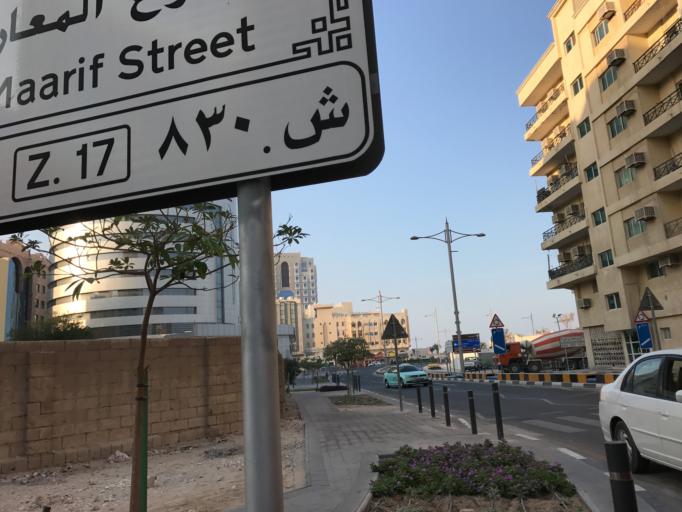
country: QA
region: Baladiyat ad Dawhah
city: Doha
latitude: 25.2854
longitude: 51.5475
